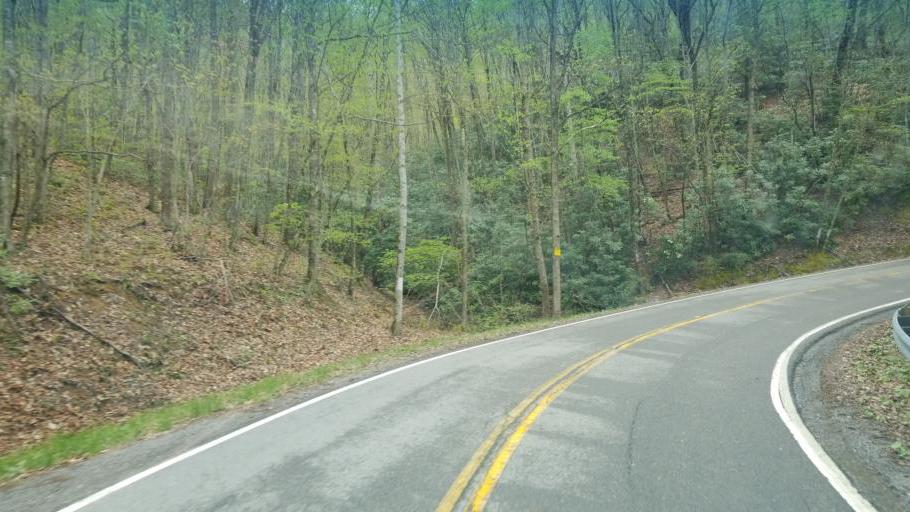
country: US
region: Virginia
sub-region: Tazewell County
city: Tazewell
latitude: 37.0070
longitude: -81.5159
